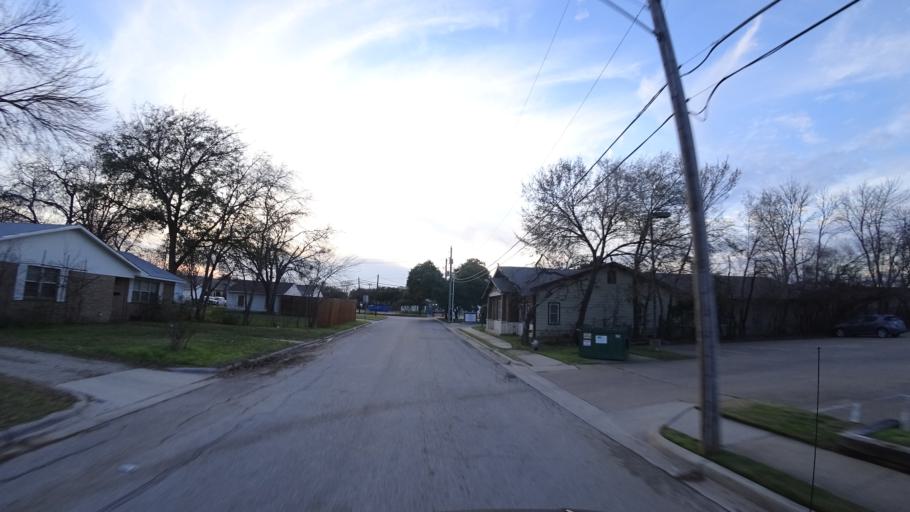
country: US
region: Texas
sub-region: Denton County
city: Lewisville
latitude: 33.0456
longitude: -97.0004
